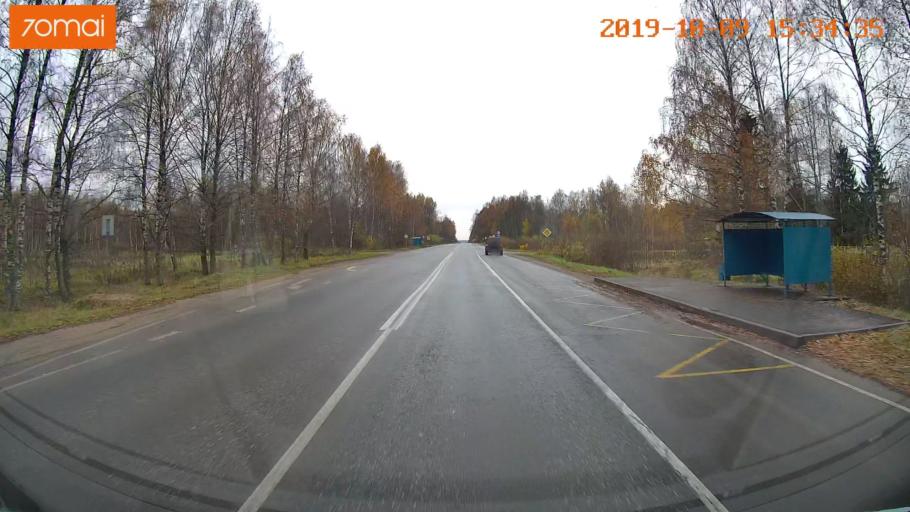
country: RU
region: Kostroma
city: Oktyabr'skiy
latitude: 57.9395
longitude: 41.2421
